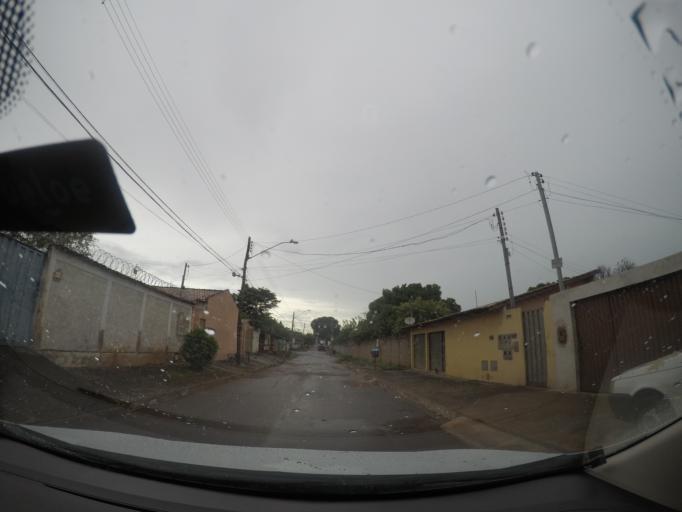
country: BR
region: Goias
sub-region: Goiania
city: Goiania
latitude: -16.6975
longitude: -49.3182
